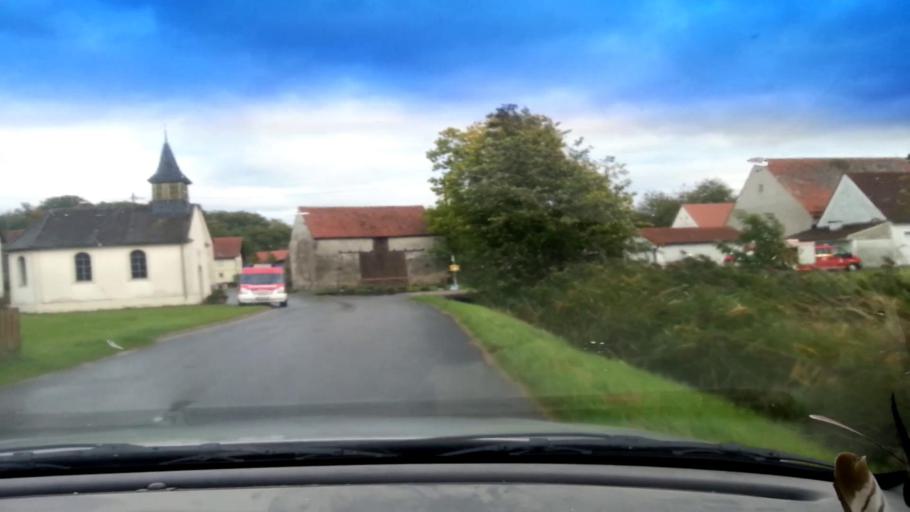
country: DE
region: Bavaria
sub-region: Upper Franconia
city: Burgebrach
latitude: 49.8081
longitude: 10.7001
